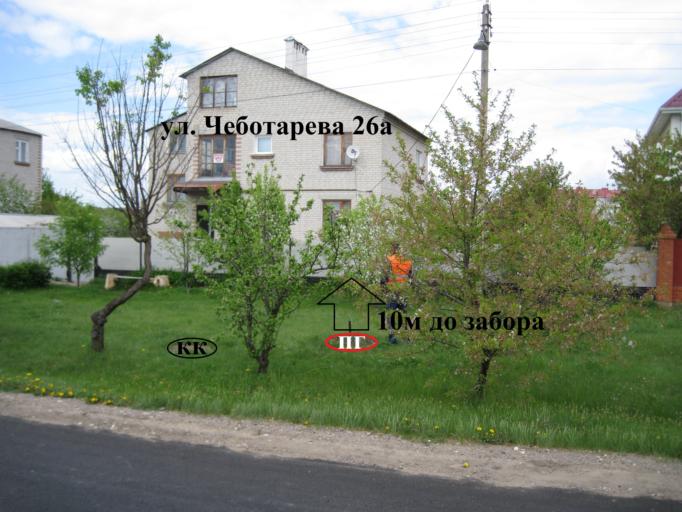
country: RU
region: Voronezj
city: Voronezh
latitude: 51.6318
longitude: 39.1596
